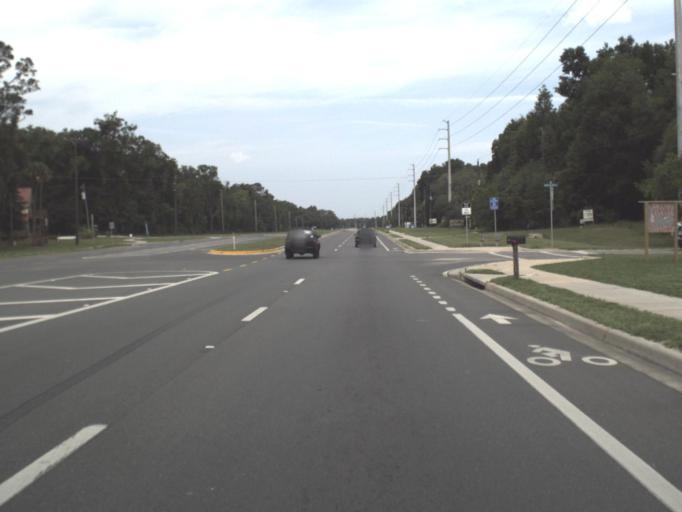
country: US
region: Florida
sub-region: Putnam County
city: Interlachen
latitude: 29.6274
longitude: -81.8642
